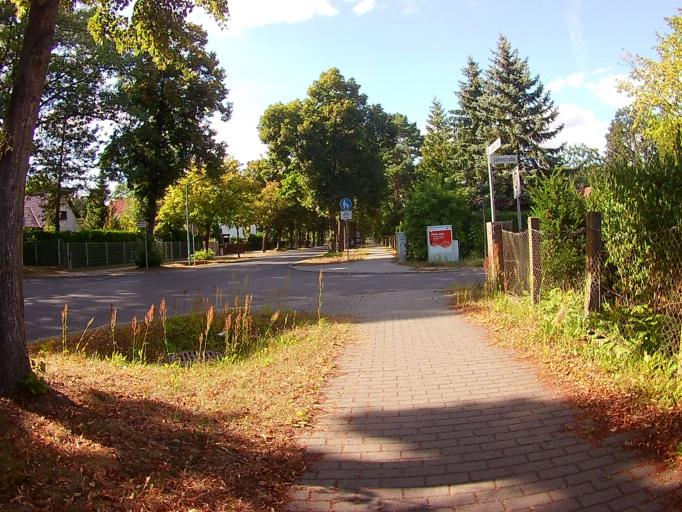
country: DE
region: Brandenburg
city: Zeuthen
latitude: 52.3746
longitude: 13.6009
